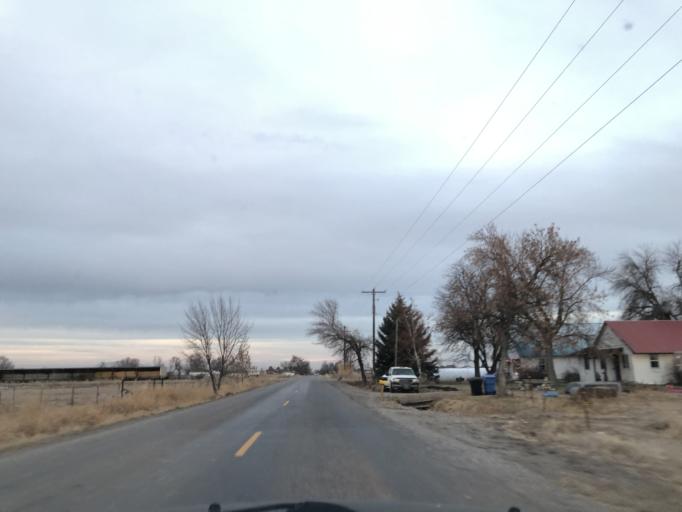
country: US
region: Utah
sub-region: Cache County
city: Benson
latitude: 41.7820
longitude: -111.9120
